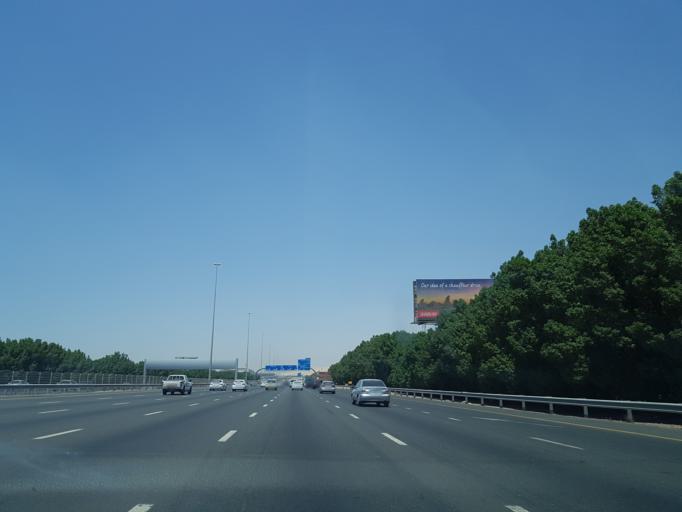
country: AE
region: Ash Shariqah
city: Sharjah
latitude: 25.2667
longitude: 55.4123
